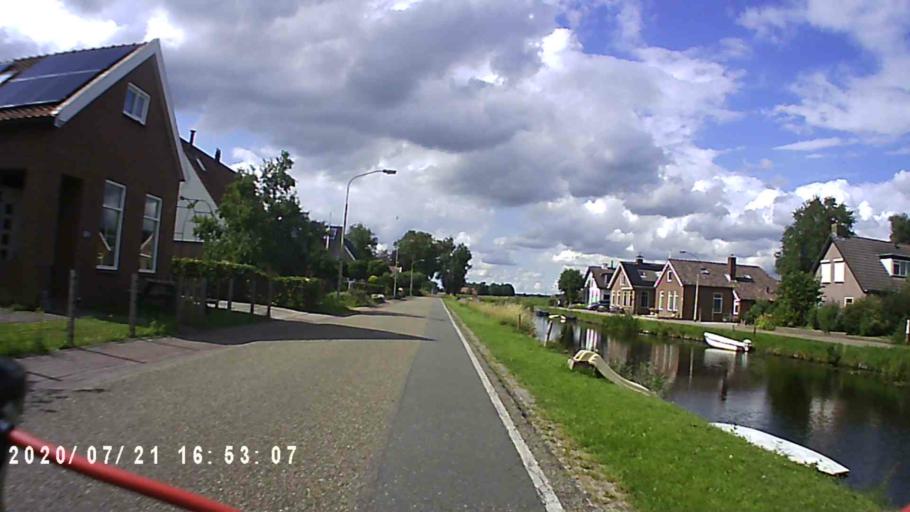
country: NL
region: Groningen
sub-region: Gemeente Hoogezand-Sappemeer
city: Hoogezand
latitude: 53.1245
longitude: 6.7704
